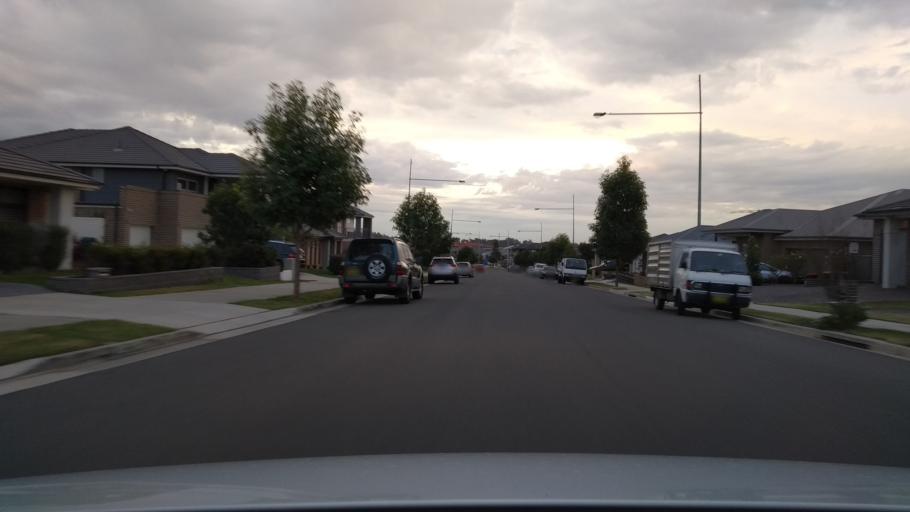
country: AU
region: New South Wales
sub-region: Camden
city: Narellan
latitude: -34.0052
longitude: 150.7353
